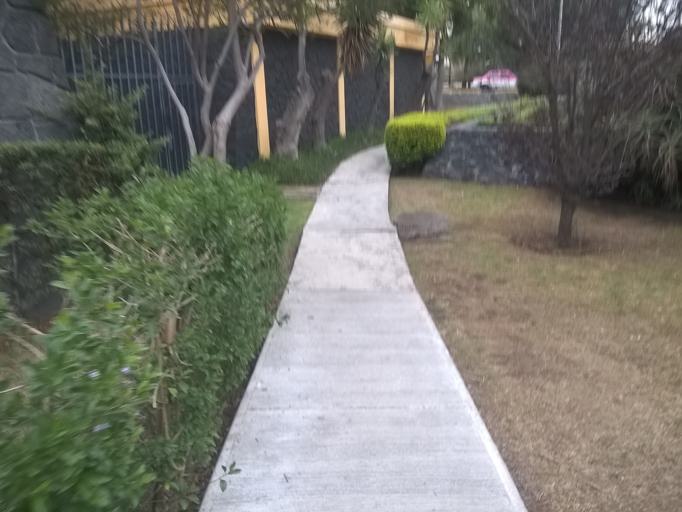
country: MX
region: Mexico City
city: Magdalena Contreras
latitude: 19.3301
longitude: -99.1866
